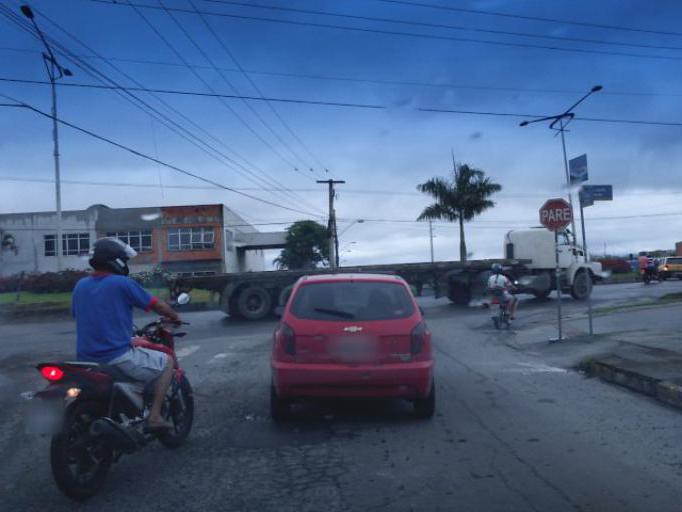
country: BR
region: Santa Catarina
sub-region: Itajai
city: Itajai
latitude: -26.9155
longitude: -48.7009
